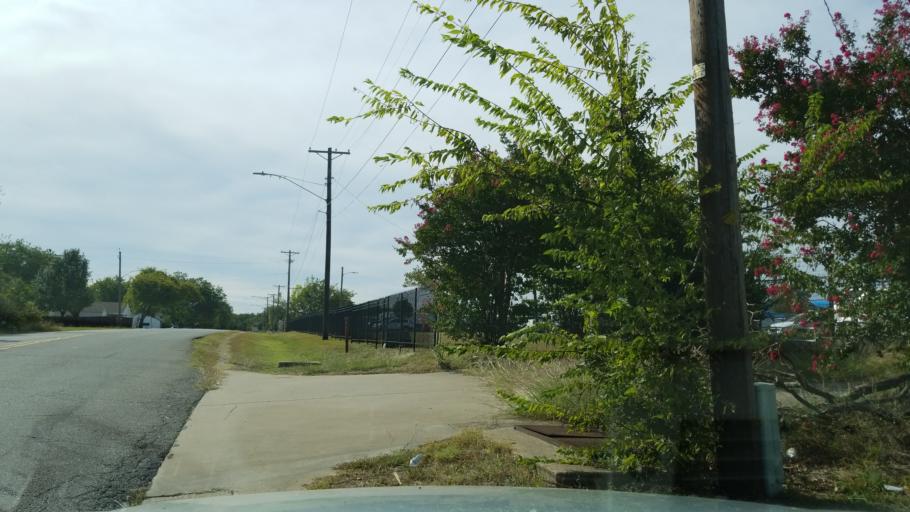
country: US
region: Texas
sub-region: Dallas County
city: Garland
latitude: 32.9085
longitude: -96.6531
